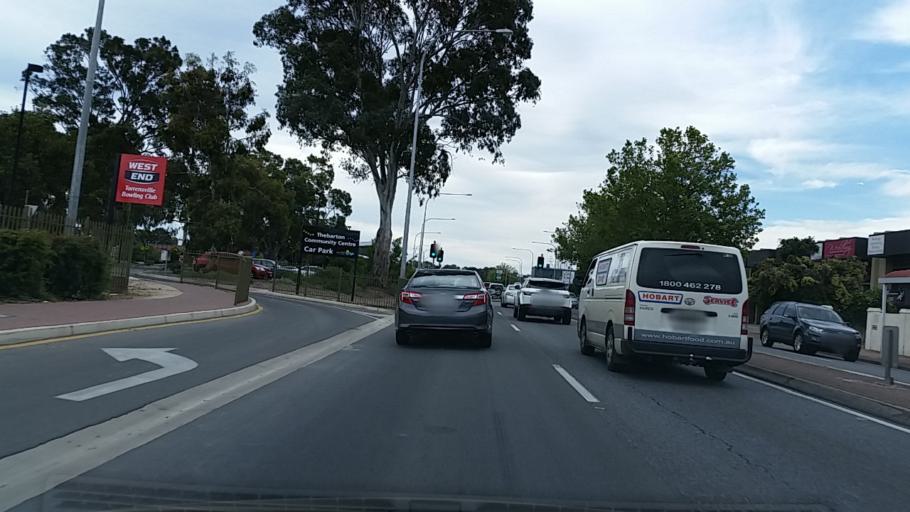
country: AU
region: South Australia
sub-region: City of West Torrens
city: Thebarton
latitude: -34.9168
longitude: 138.5670
